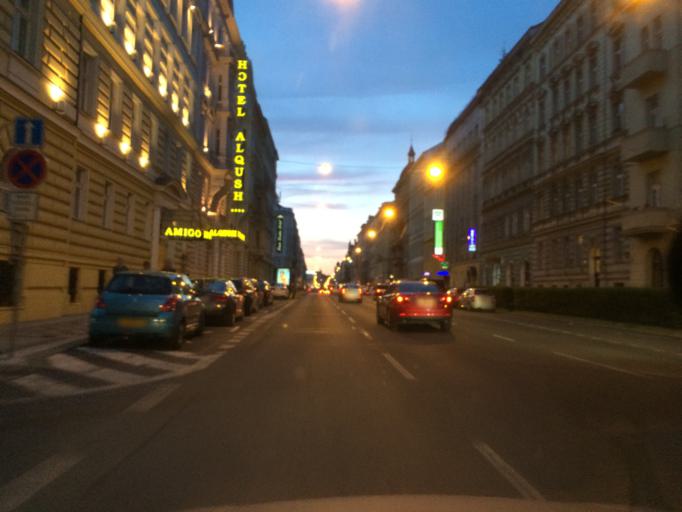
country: CZ
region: Praha
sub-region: Praha 2
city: Vysehrad
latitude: 50.0708
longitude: 14.4308
